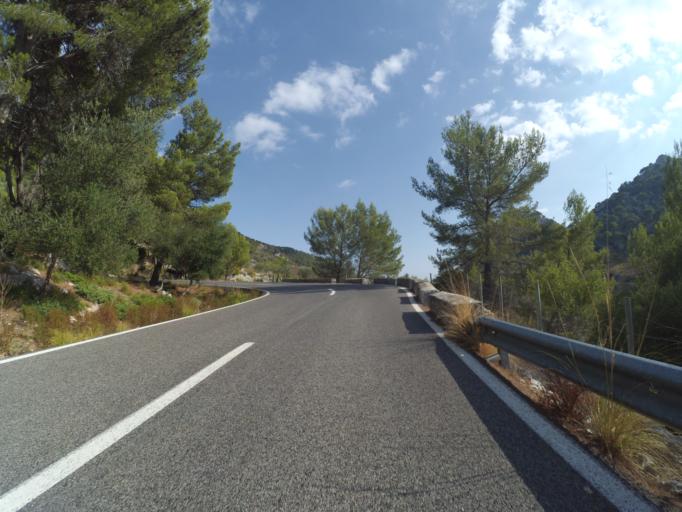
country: ES
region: Balearic Islands
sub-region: Illes Balears
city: Selva
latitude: 39.7892
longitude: 2.8932
